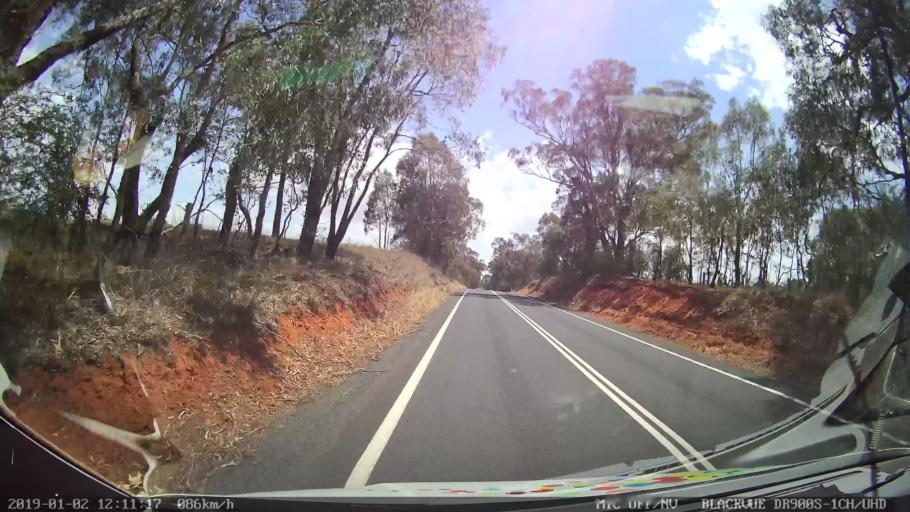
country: AU
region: New South Wales
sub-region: Young
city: Young
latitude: -34.4509
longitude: 148.2577
